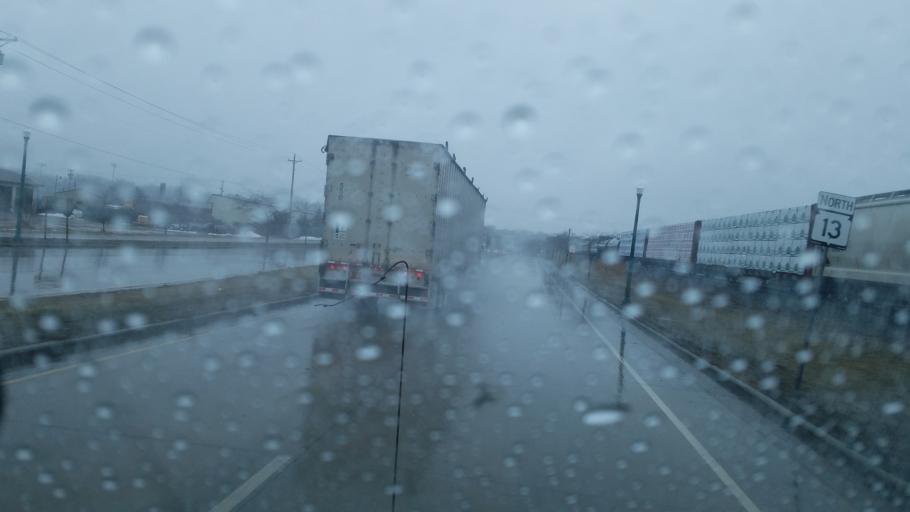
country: US
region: Wisconsin
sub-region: Wood County
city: Marshfield
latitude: 44.6678
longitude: -90.1753
